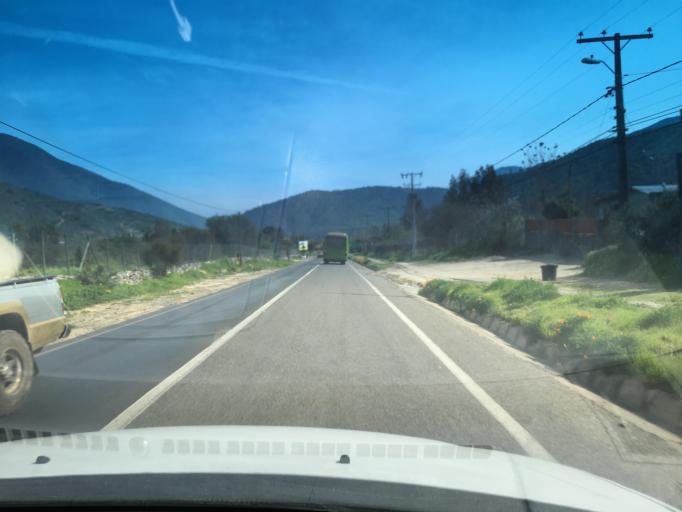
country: CL
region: Valparaiso
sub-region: Provincia de Marga Marga
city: Limache
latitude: -33.0561
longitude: -71.0878
